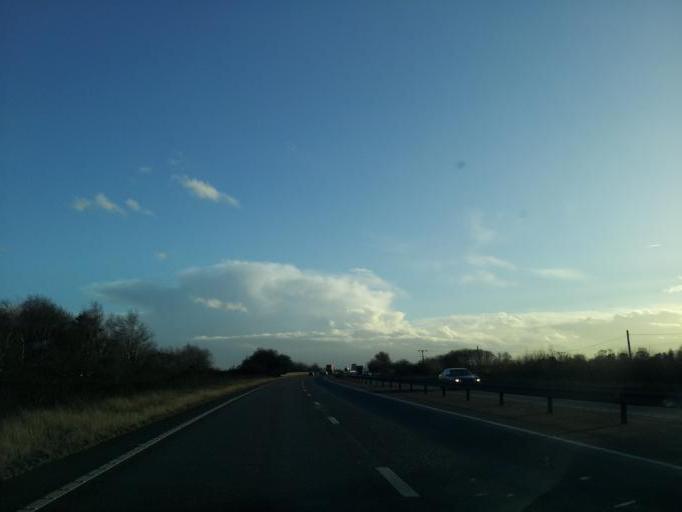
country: GB
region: England
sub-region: Nottinghamshire
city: Newark on Trent
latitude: 53.0608
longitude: -0.7653
